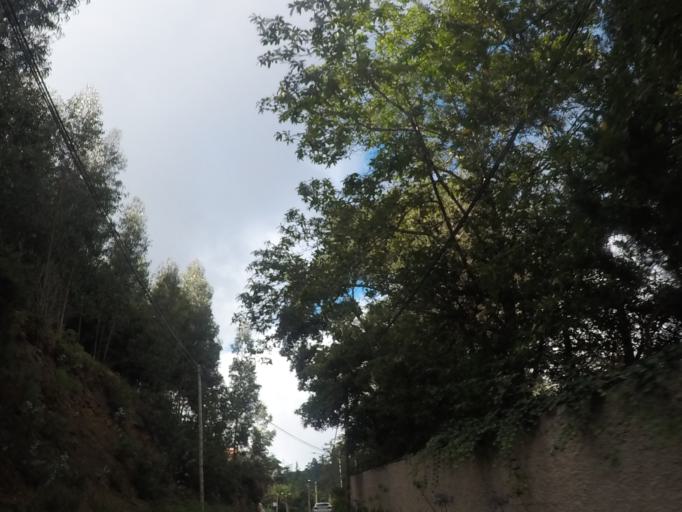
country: PT
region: Madeira
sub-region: Santa Cruz
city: Camacha
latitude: 32.6789
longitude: -16.8529
